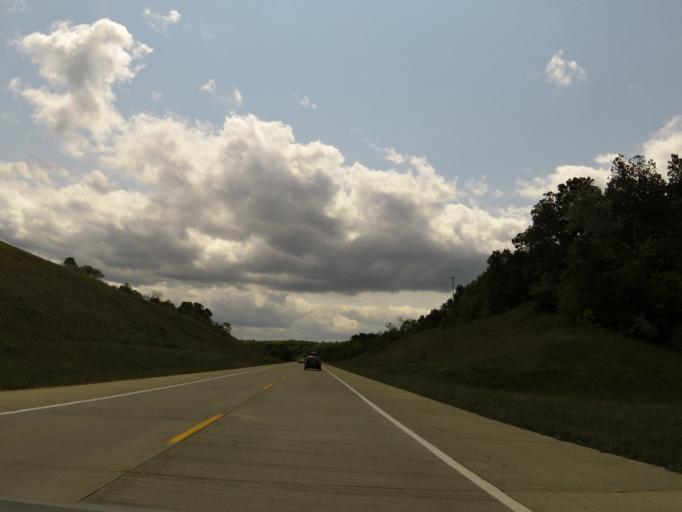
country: US
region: Ohio
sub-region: Athens County
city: Athens
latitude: 39.2238
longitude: -82.0660
